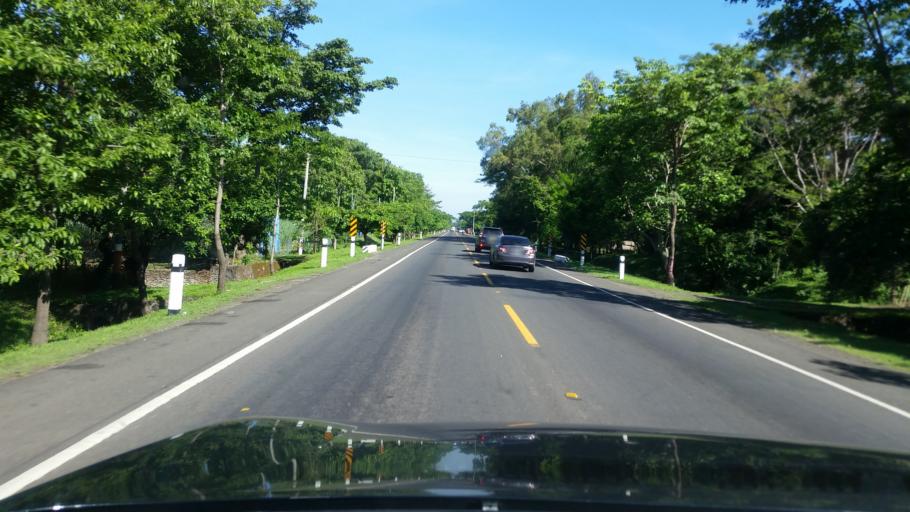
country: NI
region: Chinandega
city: Chichigalpa
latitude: 12.5954
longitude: -87.0321
